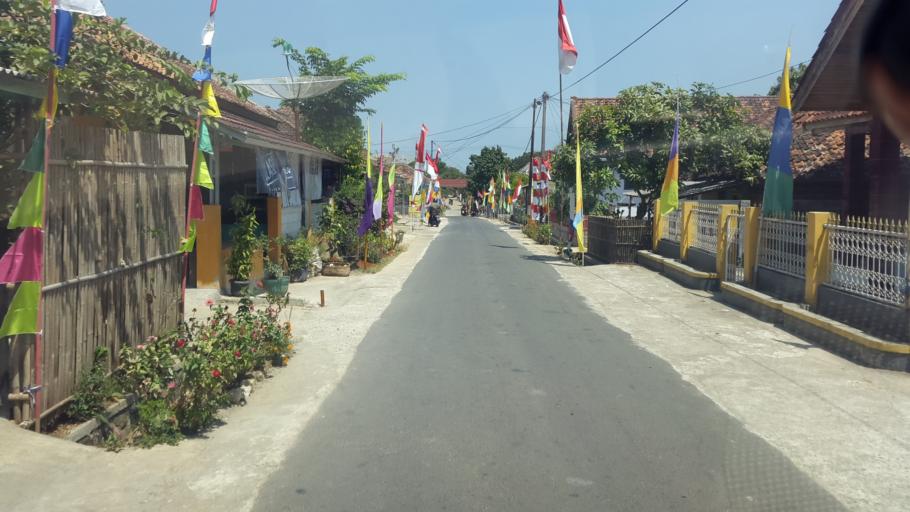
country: ID
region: West Java
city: Citeureup
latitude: -7.3301
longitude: 106.5195
